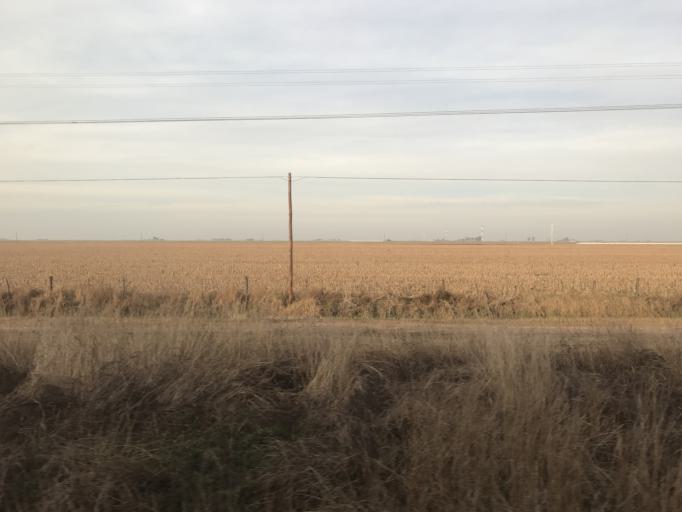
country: AR
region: Cordoba
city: Marcos Juarez
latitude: -32.6848
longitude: -62.1854
